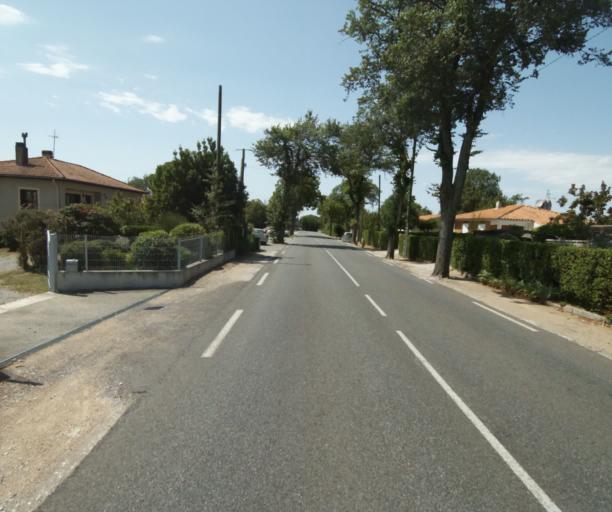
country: FR
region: Midi-Pyrenees
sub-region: Departement de la Haute-Garonne
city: Saint-Felix-Lauragais
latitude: 43.4508
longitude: 1.8821
